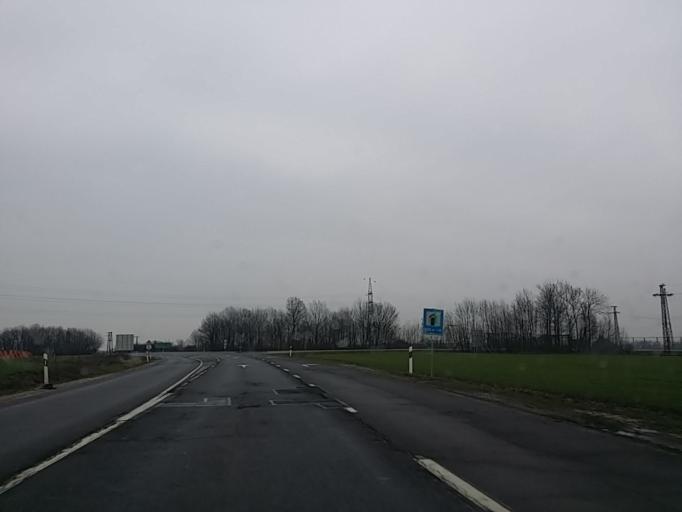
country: HU
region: Borsod-Abauj-Zemplen
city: Mezokovesd
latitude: 47.8222
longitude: 20.5969
